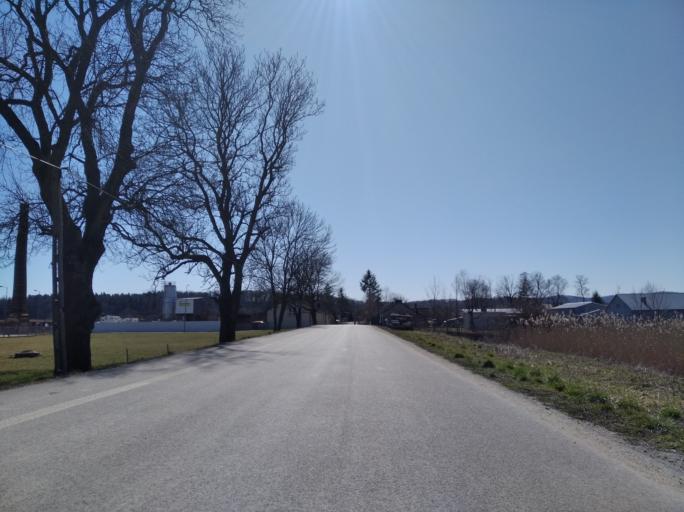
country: PL
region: Subcarpathian Voivodeship
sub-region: Powiat strzyzowski
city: Strzyzow
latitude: 49.8725
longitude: 21.7538
